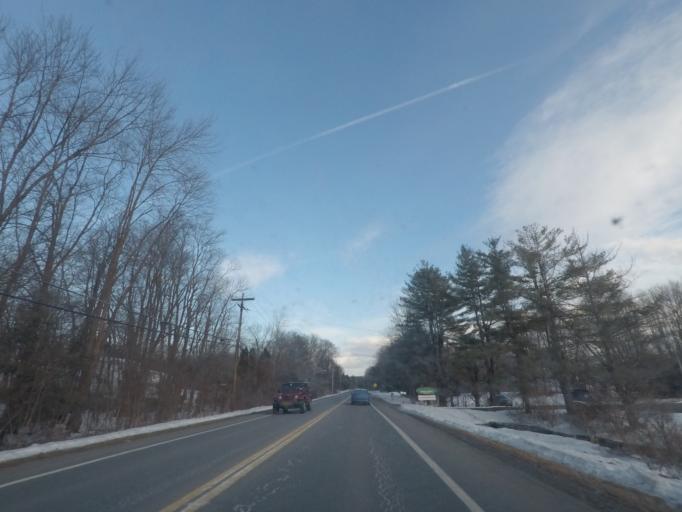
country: US
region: New York
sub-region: Schenectady County
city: Niskayuna
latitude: 42.8402
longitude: -73.8022
